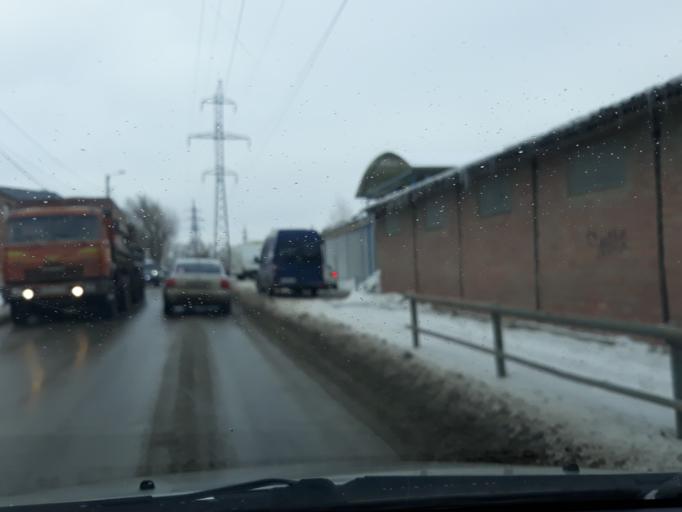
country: RU
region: Rostov
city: Taganrog
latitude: 47.2472
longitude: 38.8906
